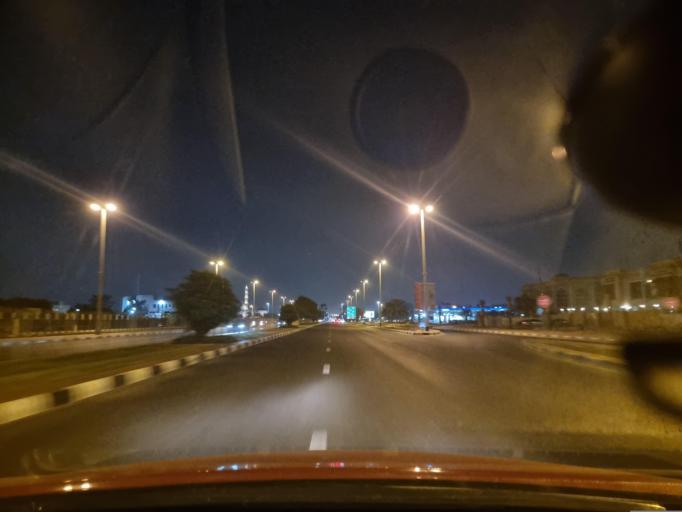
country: AE
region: Ash Shariqah
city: Sharjah
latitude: 25.3543
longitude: 55.4499
